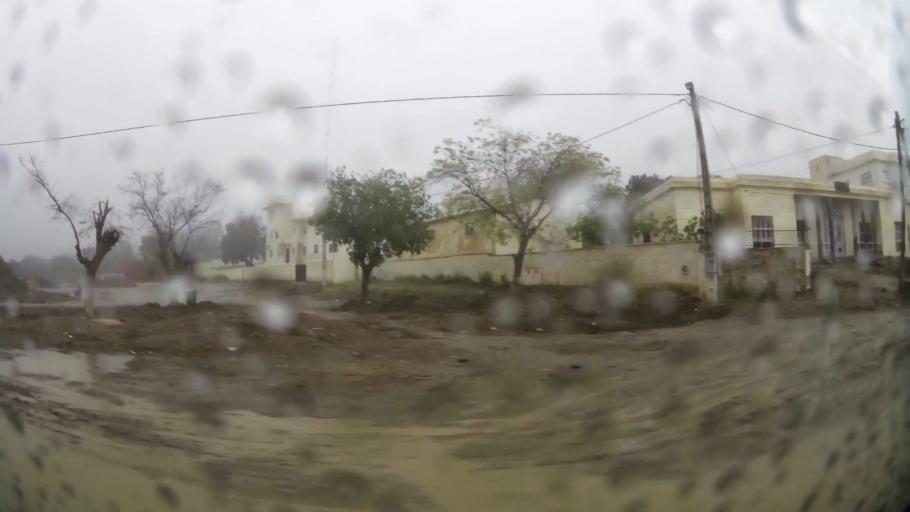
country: MA
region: Taza-Al Hoceima-Taounate
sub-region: Taza
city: Aknoul
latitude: 34.7641
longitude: -3.7937
